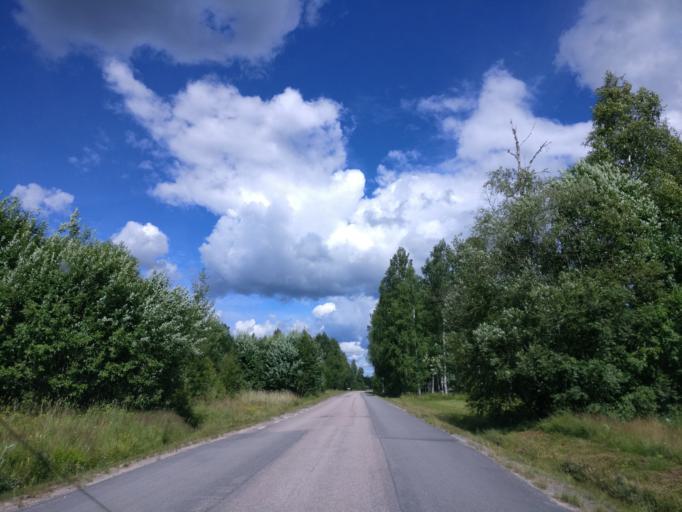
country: SE
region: Vaermland
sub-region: Hagfors Kommun
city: Ekshaerad
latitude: 60.0407
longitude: 13.4957
